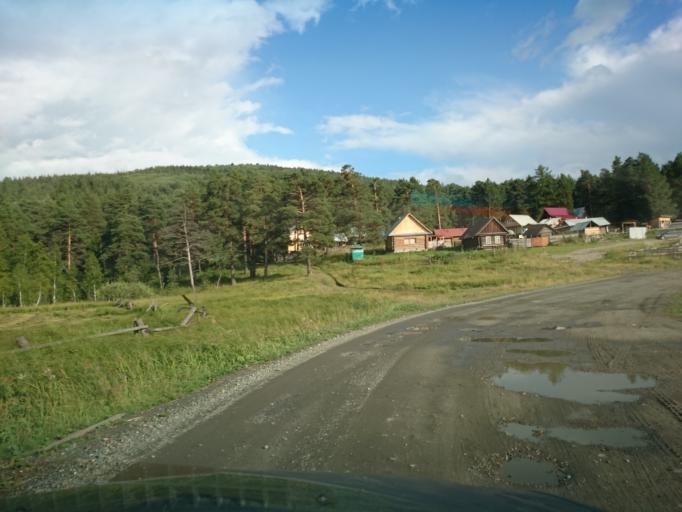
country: RU
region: Bashkortostan
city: Beloretsk
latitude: 54.0458
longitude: 58.3308
